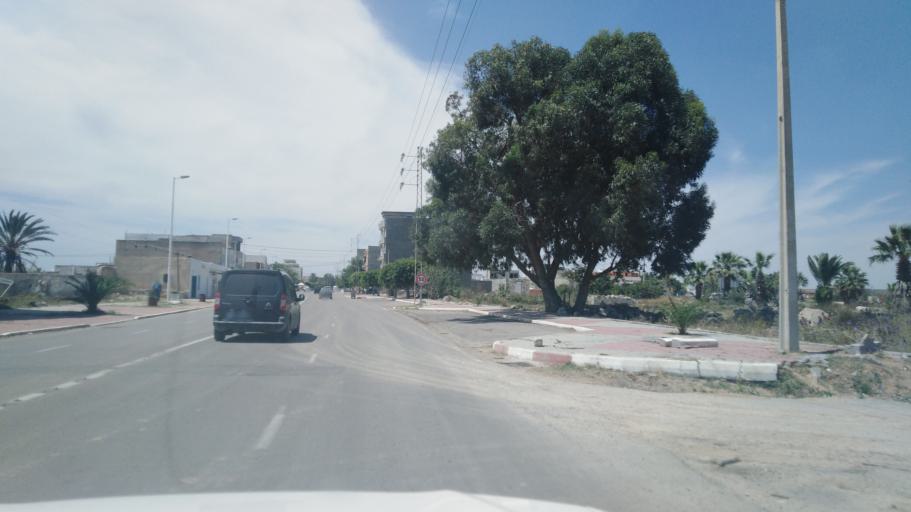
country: TN
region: Al Mahdiyah
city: Ksour Essaf
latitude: 35.4303
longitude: 11.0024
